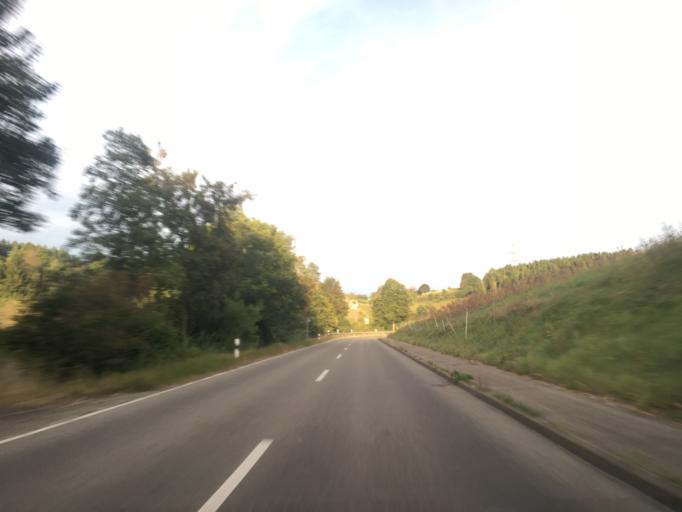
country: DE
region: Baden-Wuerttemberg
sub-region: Tuebingen Region
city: Gomadingen
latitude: 48.3782
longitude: 9.4254
